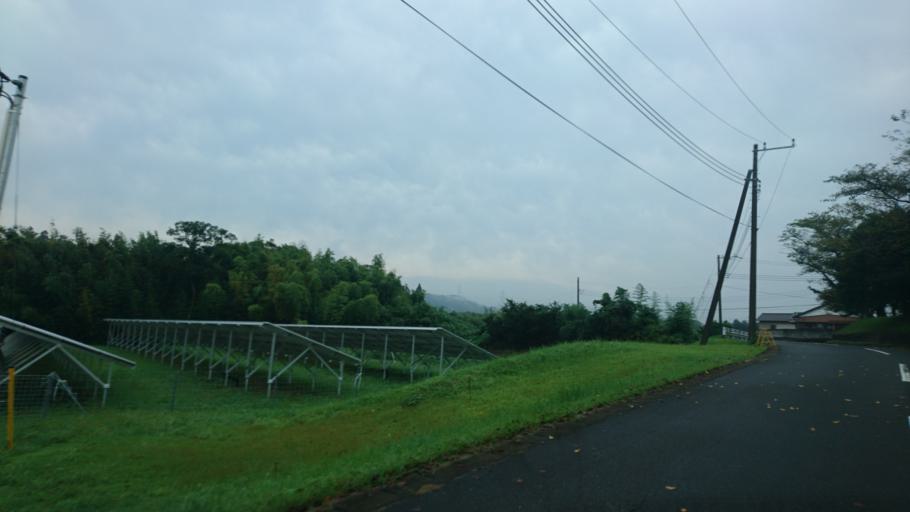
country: JP
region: Chiba
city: Kimitsu
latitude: 35.3003
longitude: 139.9807
